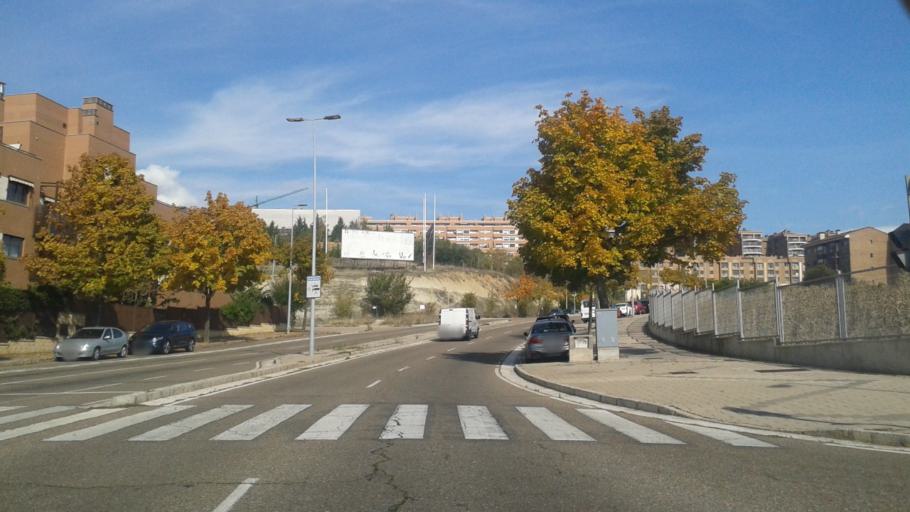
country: ES
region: Castille and Leon
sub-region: Provincia de Valladolid
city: Zaratan
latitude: 41.6325
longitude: -4.7663
